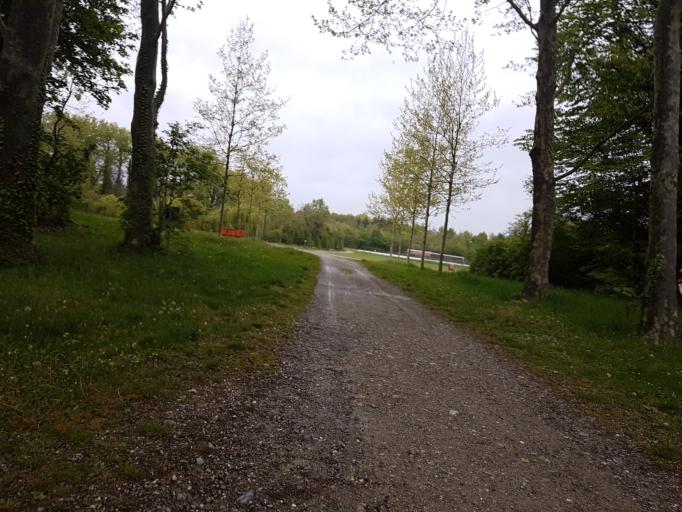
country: CH
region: Vaud
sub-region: Morges District
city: Preverenges
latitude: 46.5085
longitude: 6.5442
